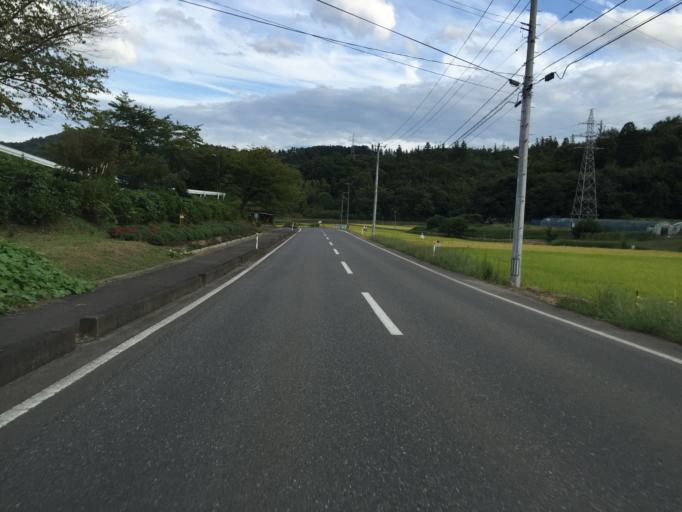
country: JP
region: Fukushima
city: Hobaramachi
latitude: 37.7855
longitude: 140.5454
